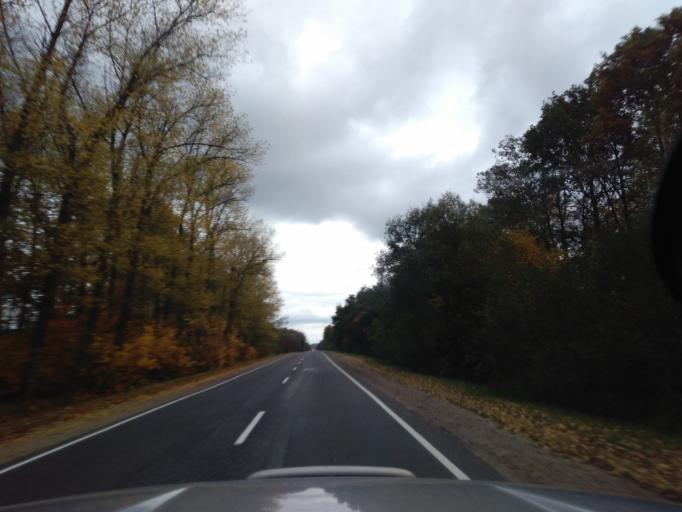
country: BY
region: Minsk
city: Slutsk
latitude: 53.2228
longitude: 27.3660
